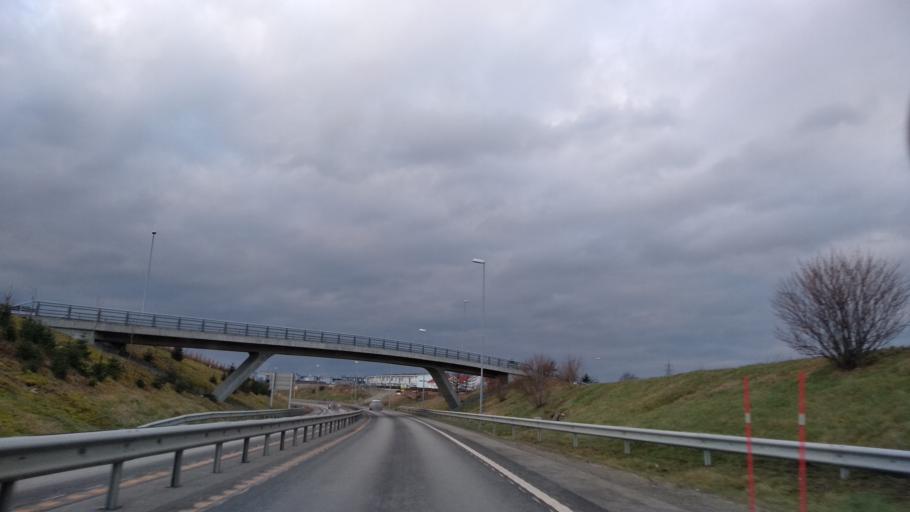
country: NO
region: Rogaland
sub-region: Klepp
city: Kleppe
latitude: 58.7844
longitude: 5.6343
